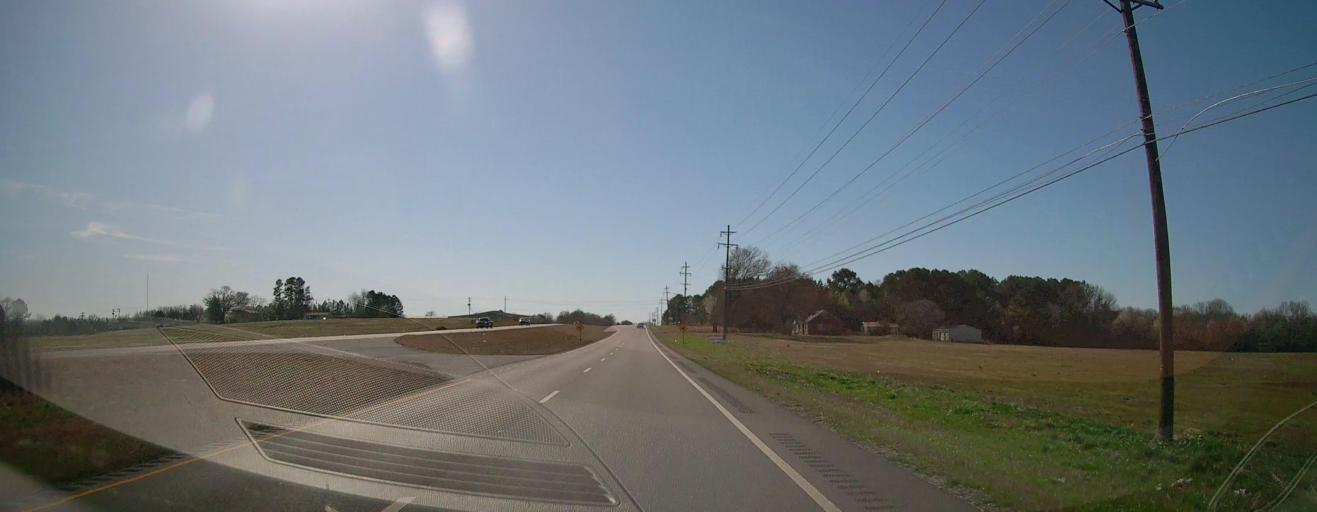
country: US
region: Alabama
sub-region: Lauderdale County
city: Killen
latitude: 34.8600
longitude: -87.4307
